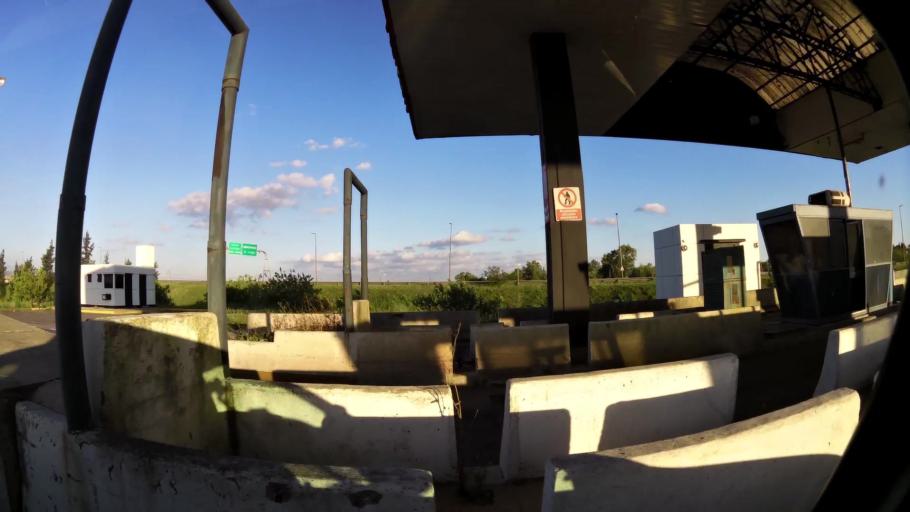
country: AR
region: Buenos Aires
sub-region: Partido de Quilmes
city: Quilmes
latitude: -34.7843
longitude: -58.1532
